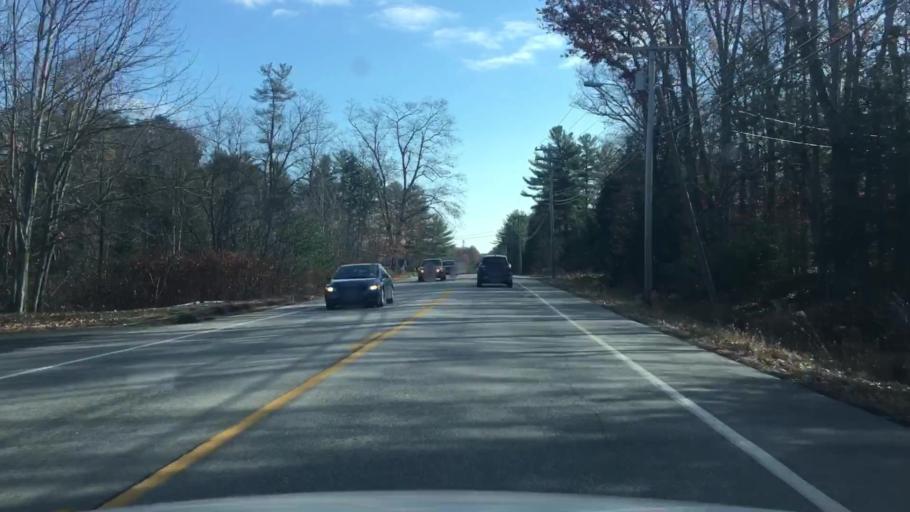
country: US
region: Maine
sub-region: Kennebec County
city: Chelsea
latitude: 44.2917
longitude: -69.7072
